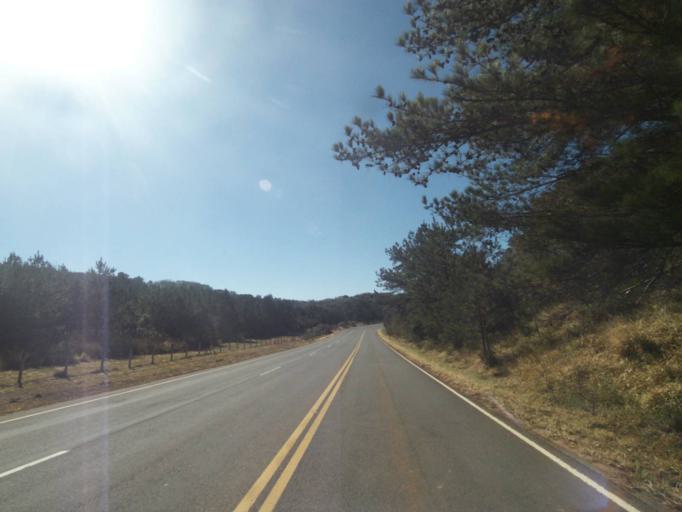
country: BR
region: Parana
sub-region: Tibagi
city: Tibagi
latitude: -24.4678
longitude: -50.4982
